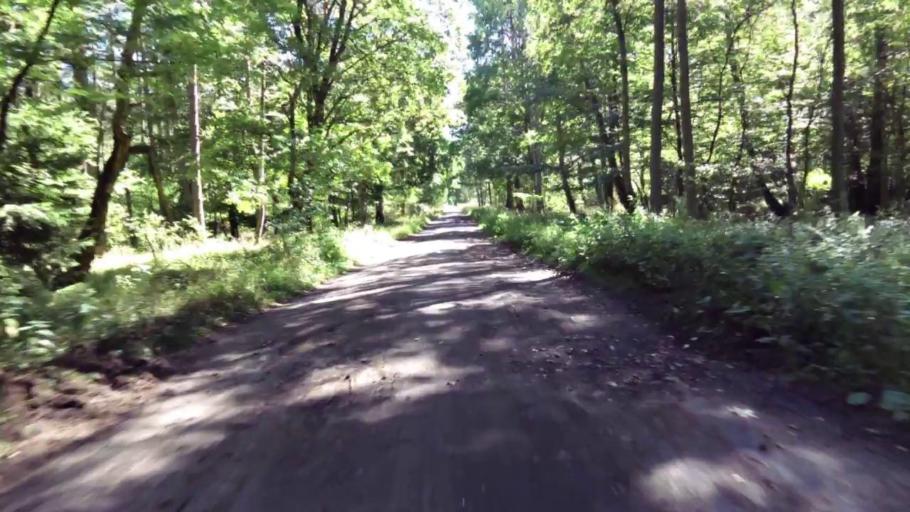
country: PL
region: West Pomeranian Voivodeship
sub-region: Powiat szczecinecki
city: Borne Sulinowo
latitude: 53.6006
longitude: 16.6105
